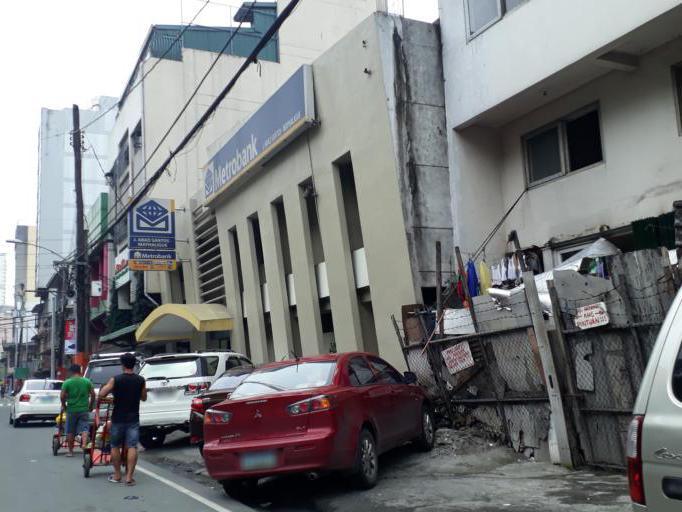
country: PH
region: Metro Manila
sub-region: City of Manila
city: Manila
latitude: 14.6098
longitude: 120.9758
